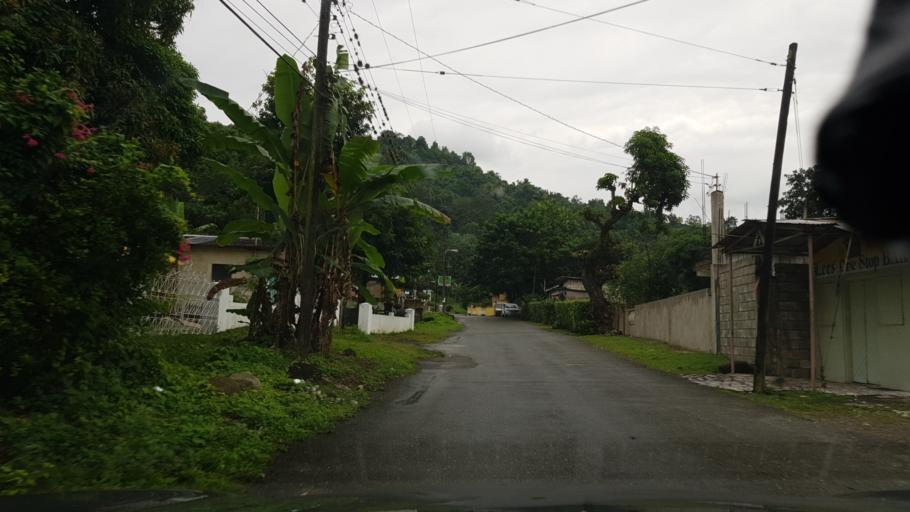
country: JM
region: Portland
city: Buff Bay
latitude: 18.2188
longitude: -76.6691
